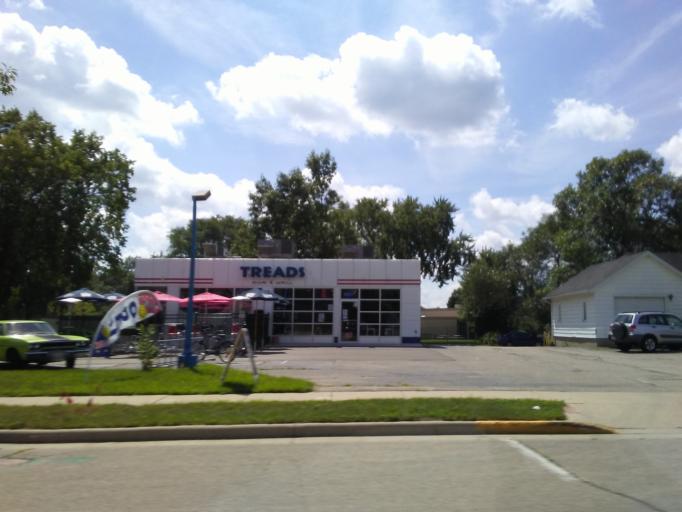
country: US
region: Wisconsin
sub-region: Dane County
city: Verona
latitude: 42.9894
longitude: -89.5392
